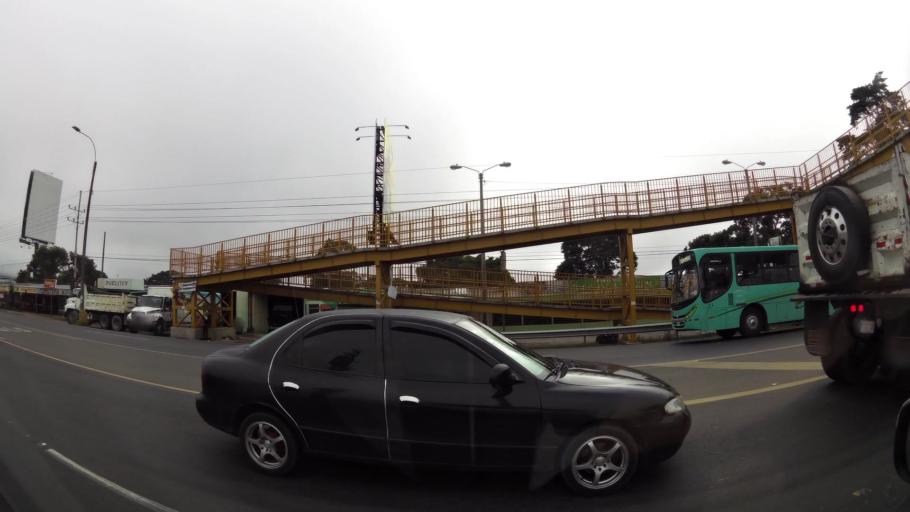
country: CR
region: Cartago
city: Cartago
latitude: 9.8712
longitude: -83.9445
